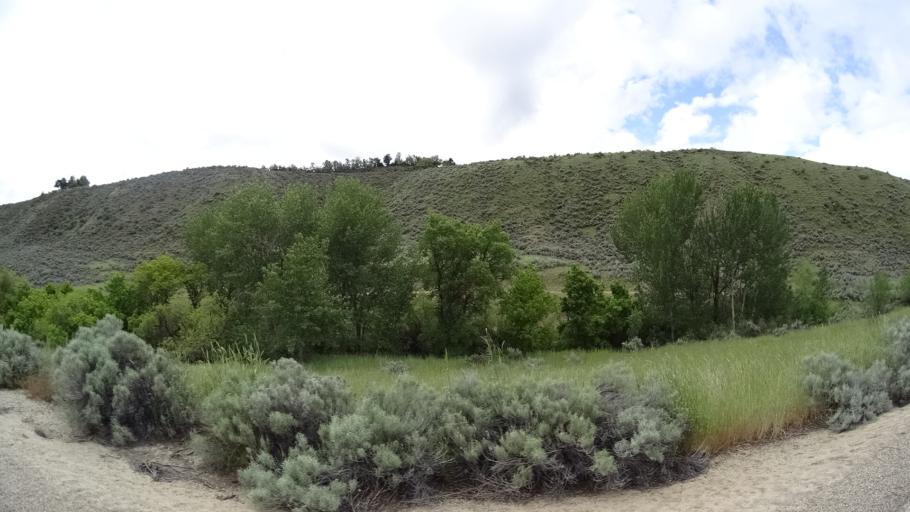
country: US
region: Idaho
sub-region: Ada County
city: Garden City
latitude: 43.6816
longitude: -116.2600
